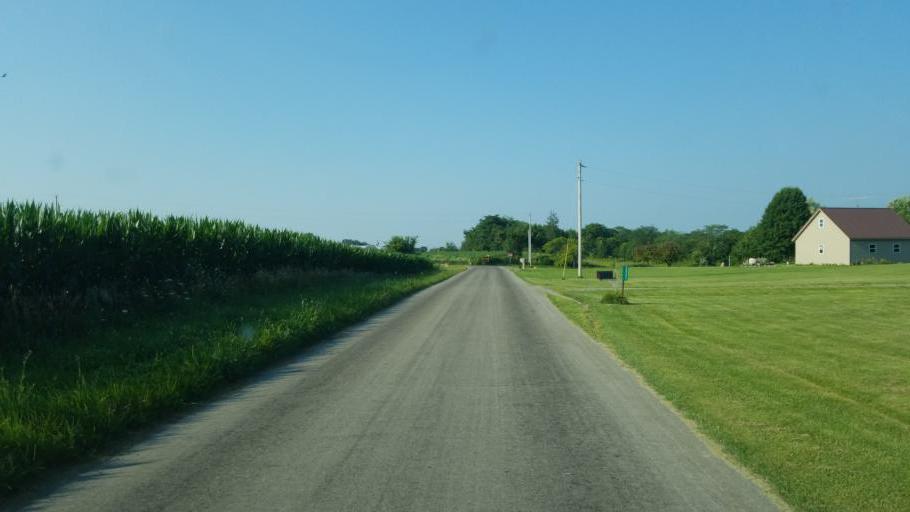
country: US
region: Ohio
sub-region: Hardin County
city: Kenton
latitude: 40.5608
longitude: -83.5844
